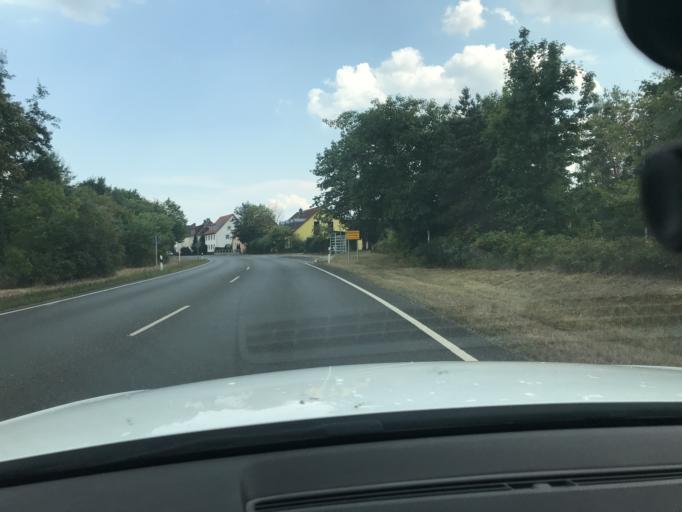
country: DE
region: Bavaria
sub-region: Upper Palatinate
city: Grafenwohr
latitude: 49.7099
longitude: 11.9253
